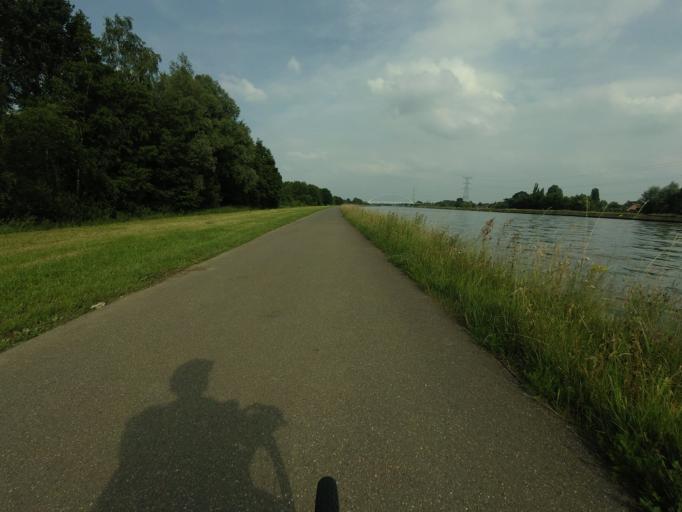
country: BE
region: Flanders
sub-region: Provincie Antwerpen
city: Zandhoven
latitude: 51.1962
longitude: 4.6469
